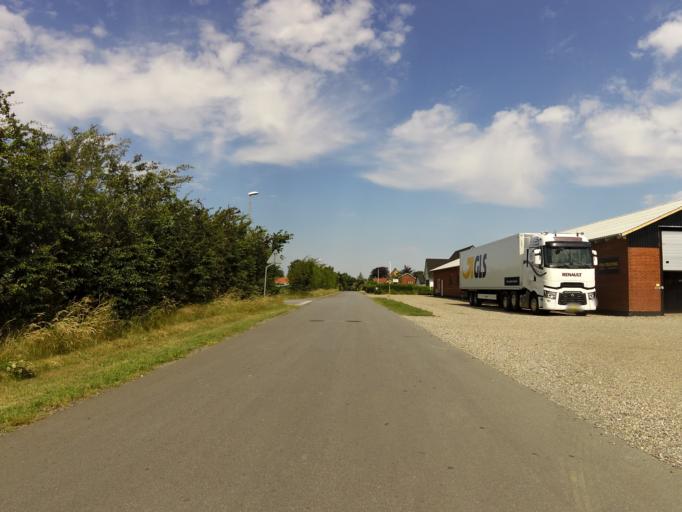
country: DK
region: South Denmark
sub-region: Haderslev Kommune
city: Vojens
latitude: 55.1958
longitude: 9.2119
